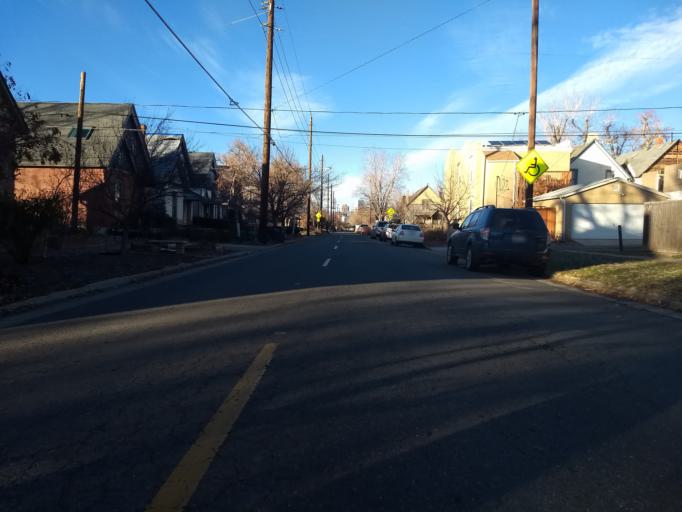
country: US
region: Colorado
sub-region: Denver County
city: Denver
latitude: 39.7124
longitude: -104.9900
